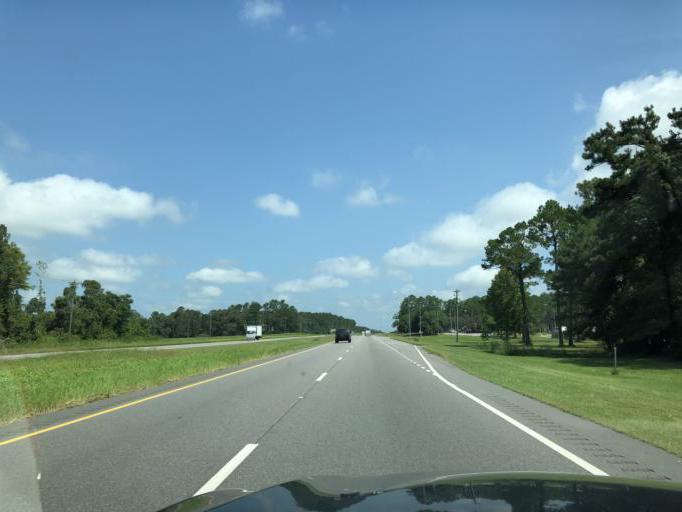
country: US
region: Alabama
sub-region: Houston County
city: Cottonwood
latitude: 31.0063
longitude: -85.4077
